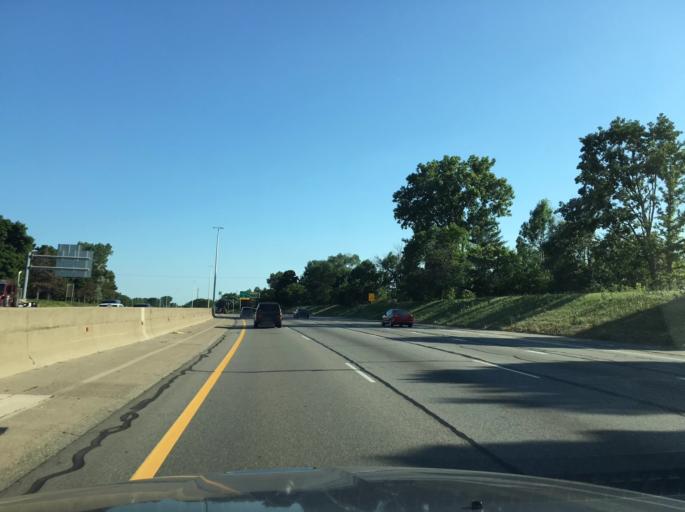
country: US
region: Michigan
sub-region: Macomb County
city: Roseville
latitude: 42.4863
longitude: -82.9175
